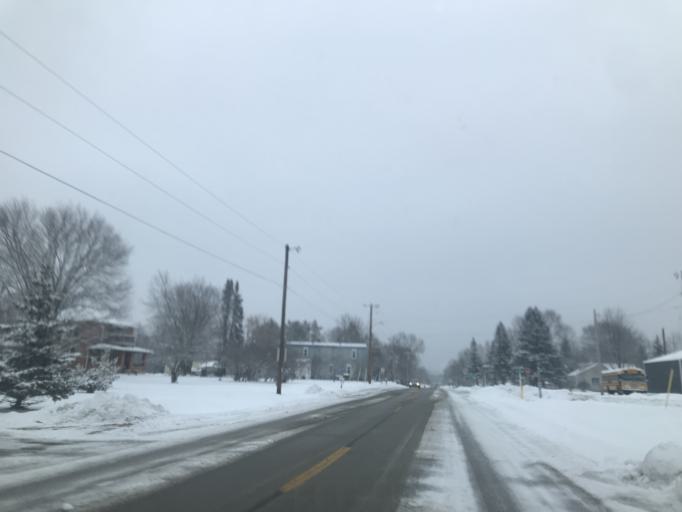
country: US
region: Wisconsin
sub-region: Oconto County
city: Oconto Falls
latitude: 44.8714
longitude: -88.1579
